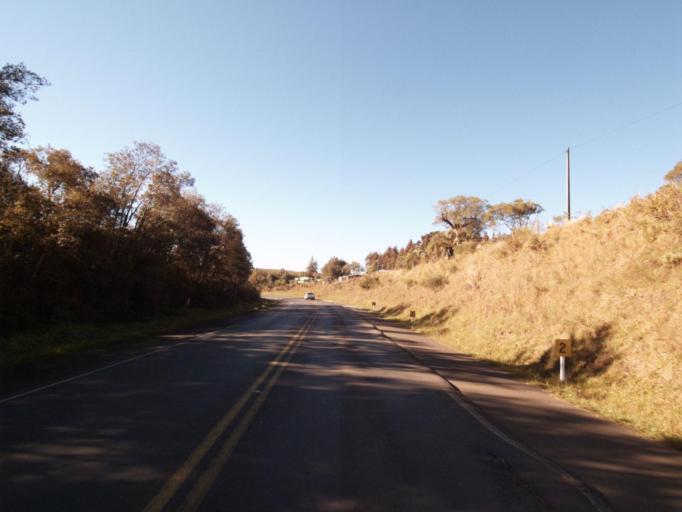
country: BR
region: Santa Catarina
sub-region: Concordia
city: Concordia
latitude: -26.9201
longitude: -51.9538
